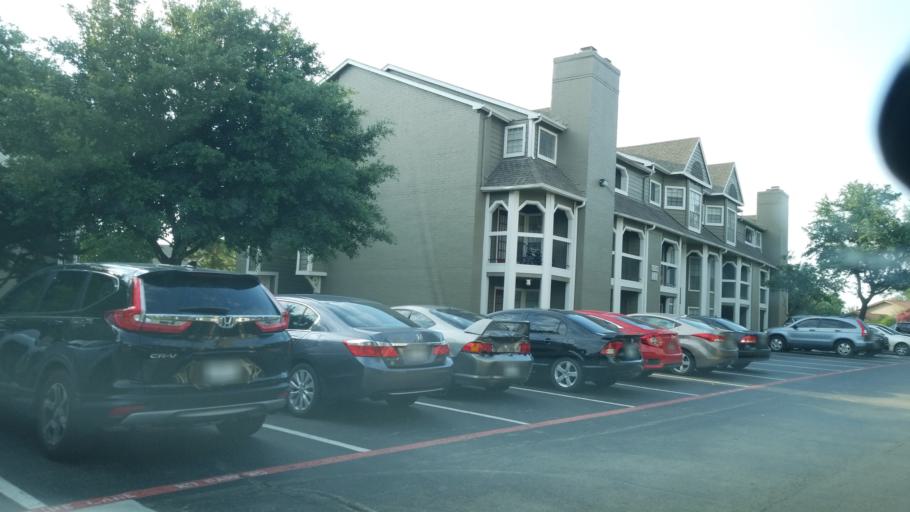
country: US
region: Texas
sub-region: Dallas County
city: Coppell
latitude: 32.9024
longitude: -96.9649
